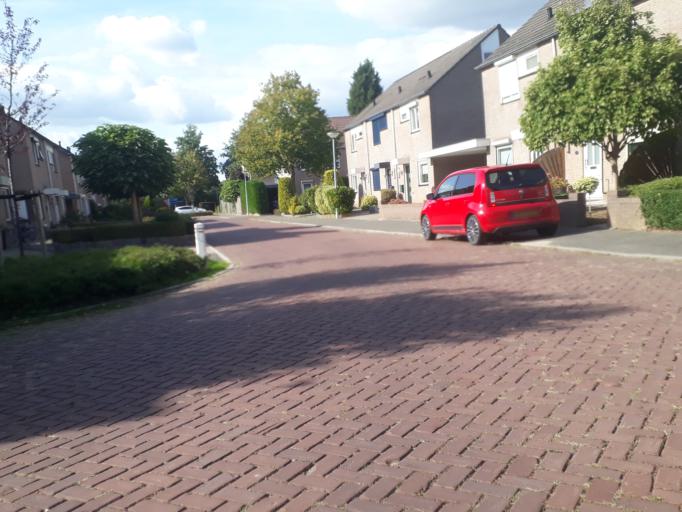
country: NL
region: Gelderland
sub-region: Gemeente Zevenaar
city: Zevenaar
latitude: 51.9300
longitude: 6.0499
